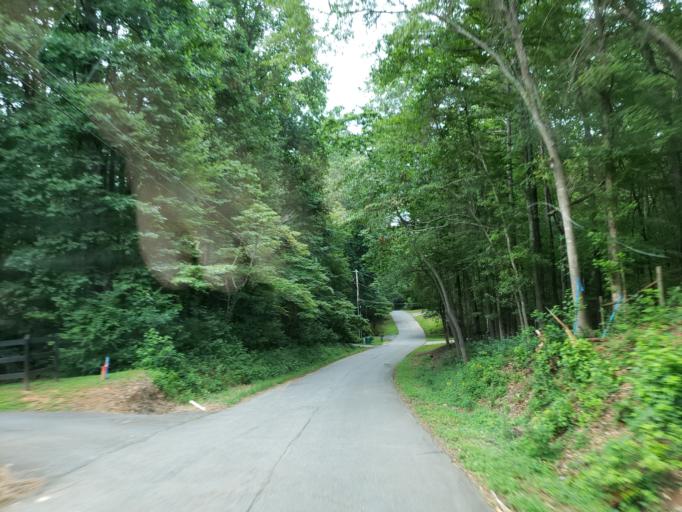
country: US
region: Georgia
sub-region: Cherokee County
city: Holly Springs
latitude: 34.1252
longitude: -84.4508
